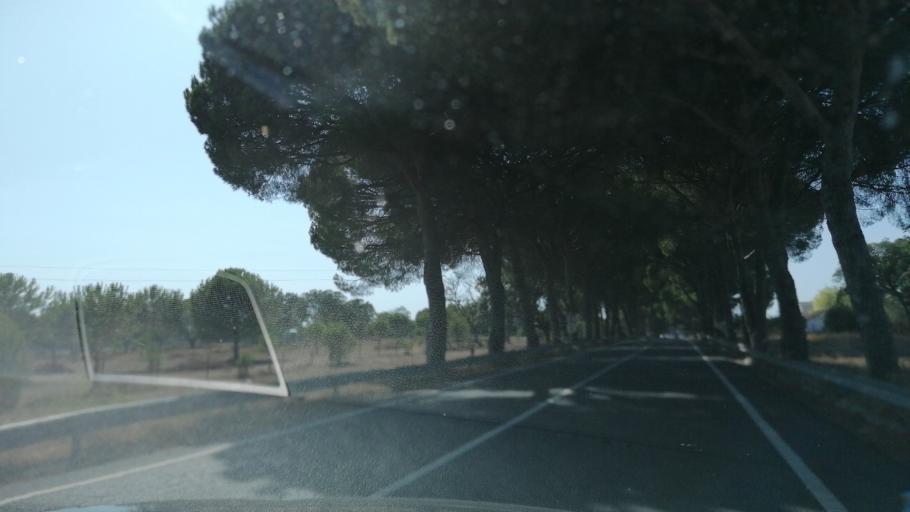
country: PT
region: Evora
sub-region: Vendas Novas
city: Vendas Novas
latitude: 38.7177
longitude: -8.6208
